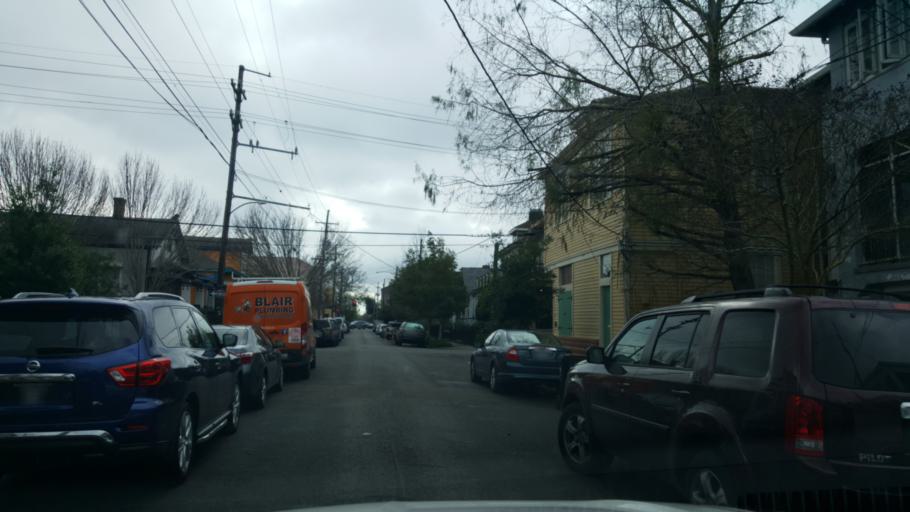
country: US
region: Louisiana
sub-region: Orleans Parish
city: New Orleans
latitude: 29.9321
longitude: -90.0757
